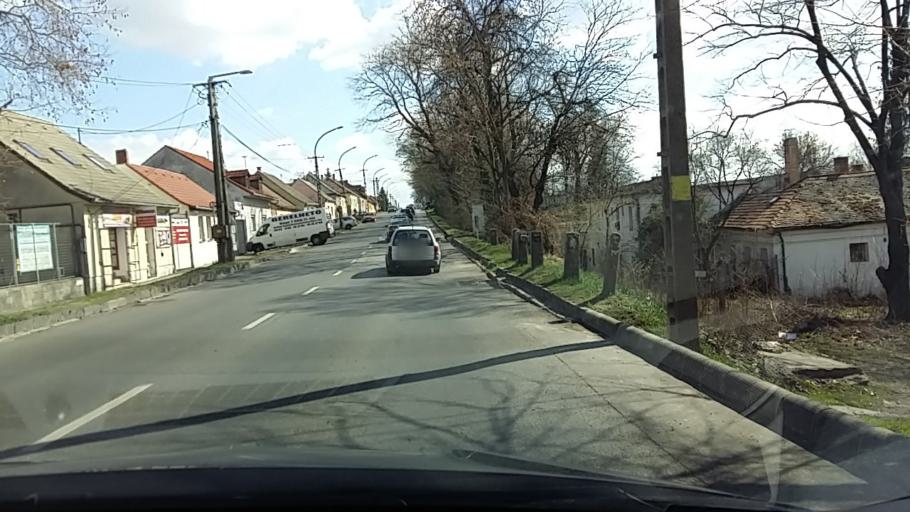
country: HU
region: Baranya
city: Pecs
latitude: 46.0805
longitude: 18.2601
